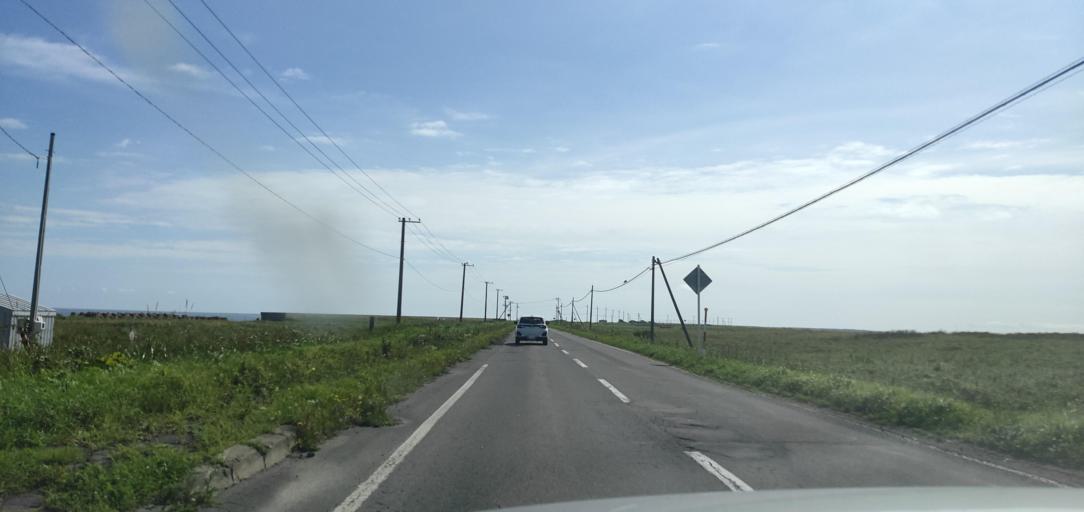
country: JP
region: Hokkaido
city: Shibetsu
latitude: 43.6280
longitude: 145.1966
